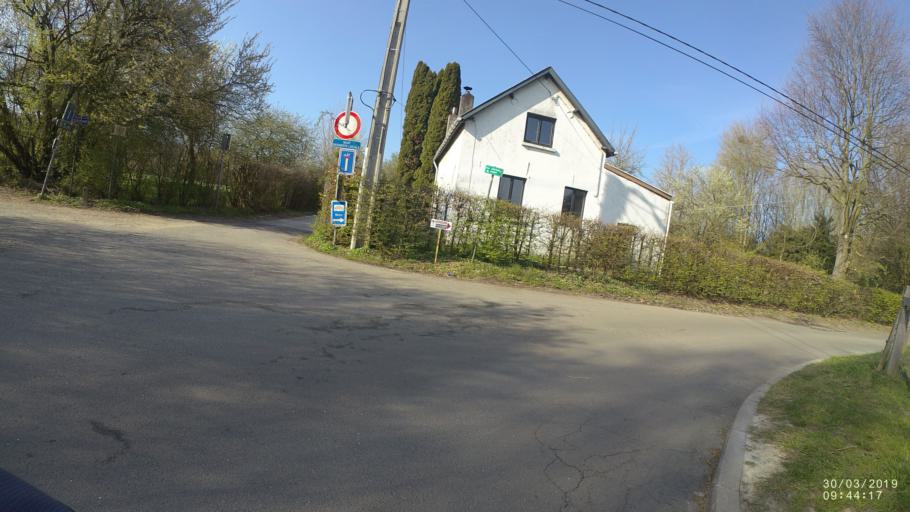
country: BE
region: Wallonia
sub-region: Province du Brabant Wallon
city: Louvain-la-Neuve
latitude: 50.6844
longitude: 4.6019
